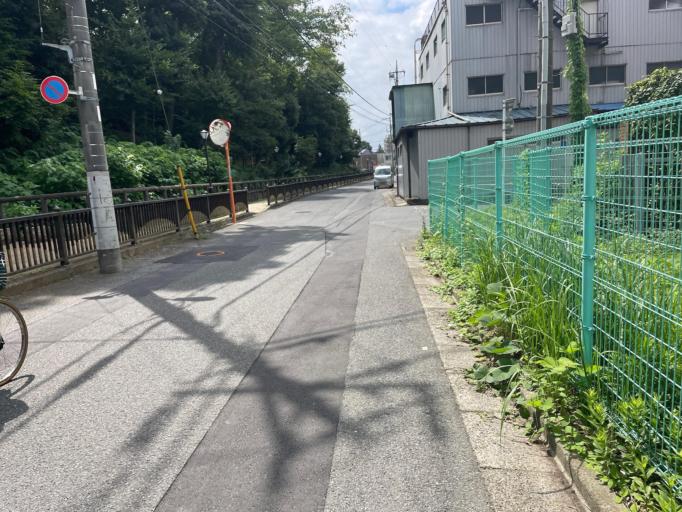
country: JP
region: Saitama
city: Wako
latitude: 35.7862
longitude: 139.6317
